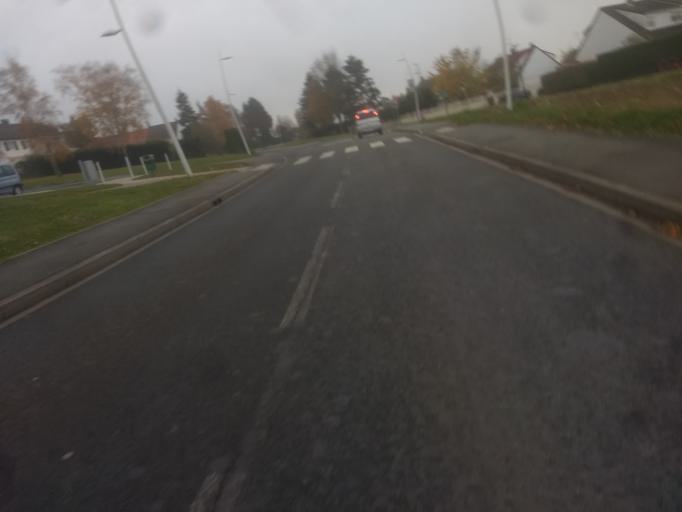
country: FR
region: Nord-Pas-de-Calais
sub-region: Departement du Pas-de-Calais
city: Saint-Laurent-Blangy
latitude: 50.3049
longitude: 2.7966
